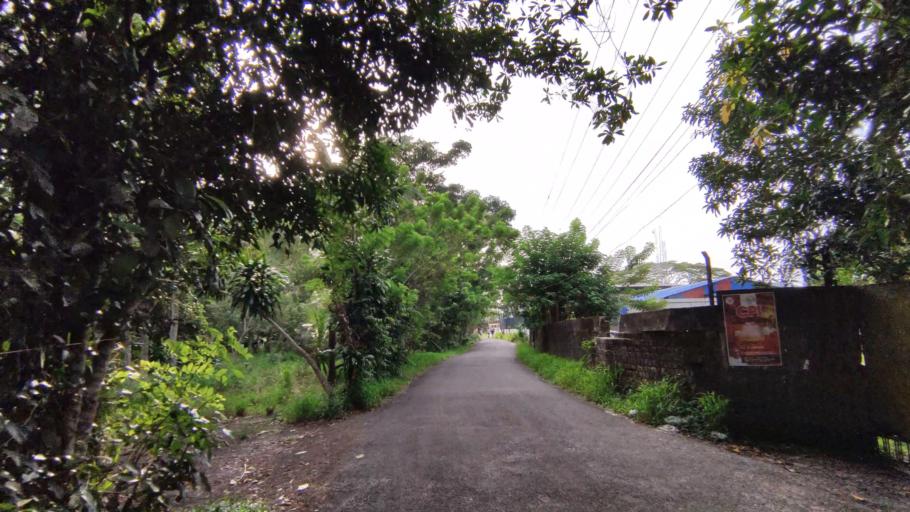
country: IN
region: Kerala
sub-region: Alappuzha
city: Shertallai
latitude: 9.6207
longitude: 76.3329
